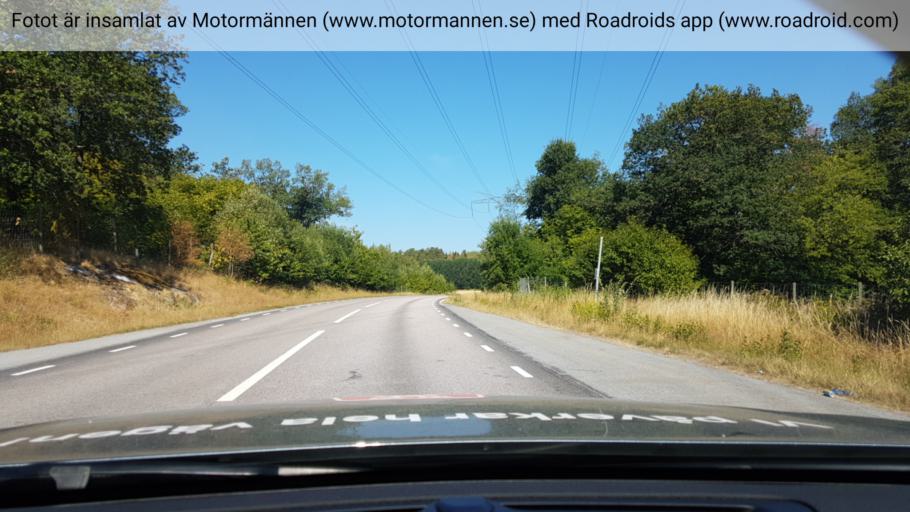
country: SE
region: Stockholm
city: Stenhamra
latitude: 59.3489
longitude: 17.6258
